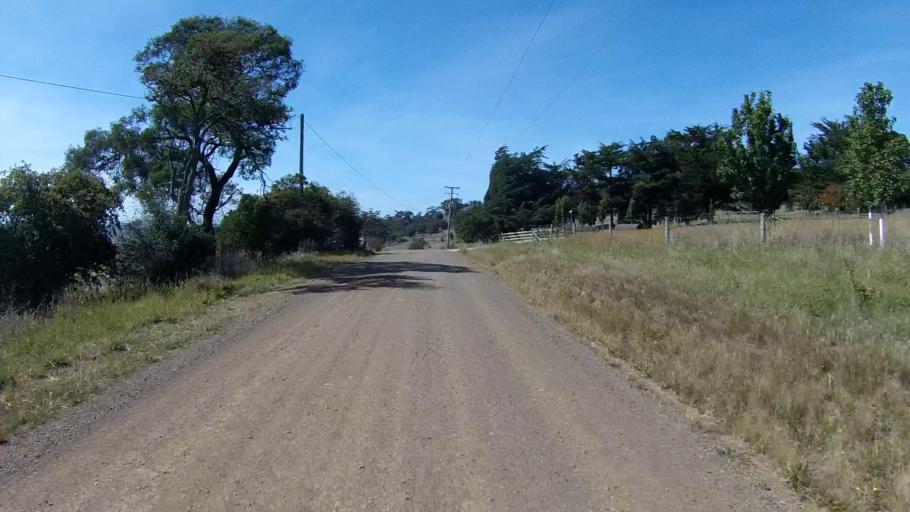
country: AU
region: Tasmania
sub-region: Sorell
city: Sorell
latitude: -42.7416
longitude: 147.5999
